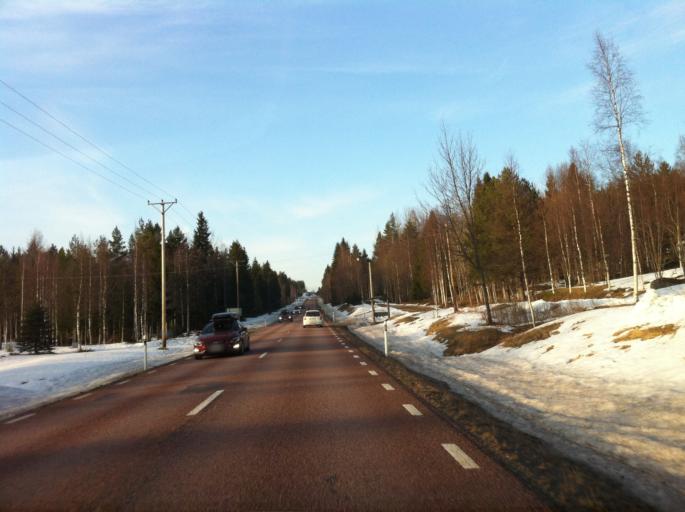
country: SE
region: Dalarna
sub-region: Vansbro Kommun
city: Vansbro
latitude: 60.2557
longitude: 14.1734
